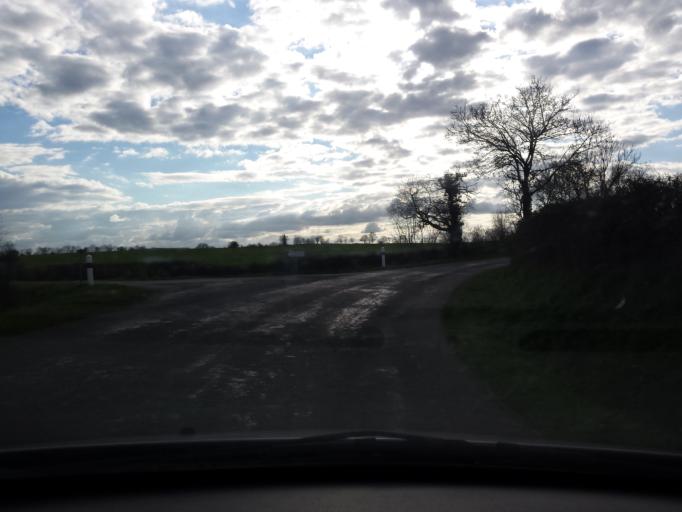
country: FR
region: Pays de la Loire
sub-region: Departement de la Vendee
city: Sainte-Cecile
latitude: 46.7215
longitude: -1.1368
